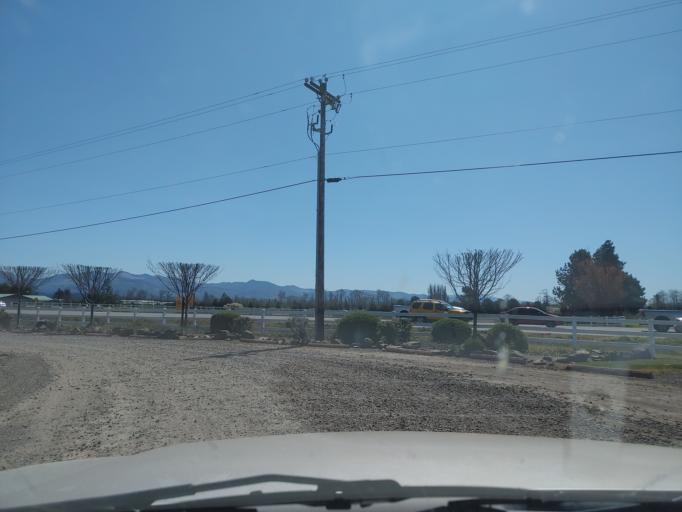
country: US
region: Oregon
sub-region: Tillamook County
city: Tillamook
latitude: 45.4822
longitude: -123.8446
